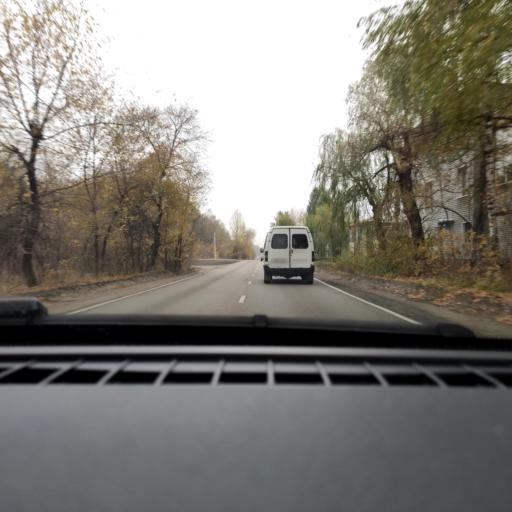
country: RU
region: Voronezj
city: Somovo
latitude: 51.7249
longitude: 39.2960
